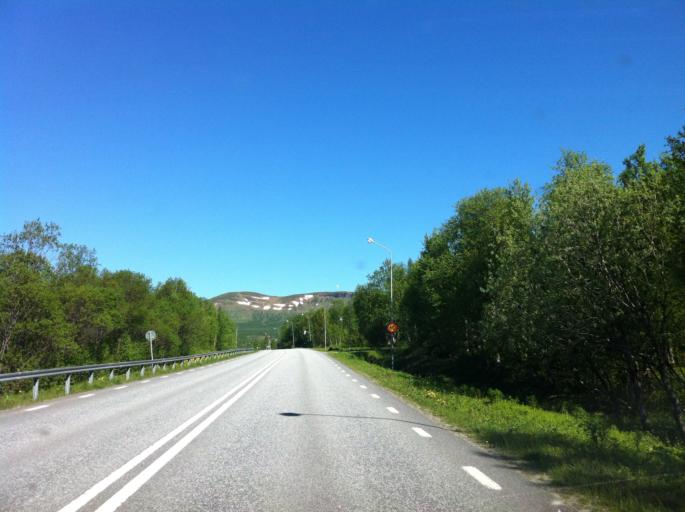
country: NO
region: Sor-Trondelag
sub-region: Tydal
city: Aas
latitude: 62.5420
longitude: 12.3362
